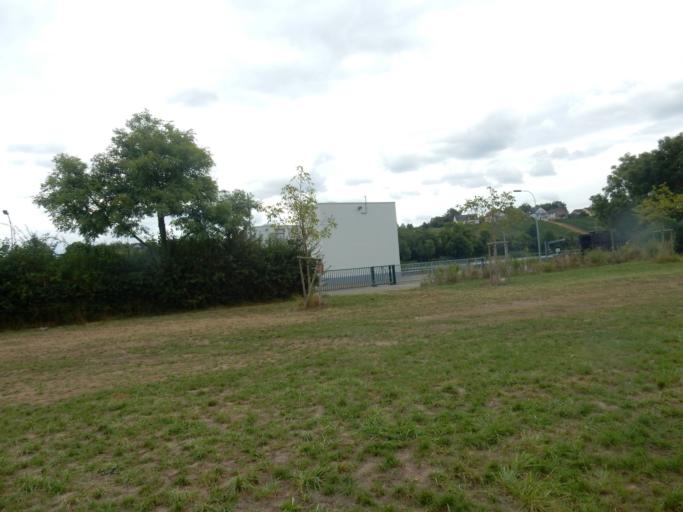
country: DE
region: Rheinland-Pfalz
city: Palzem
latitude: 49.5664
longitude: 6.3646
